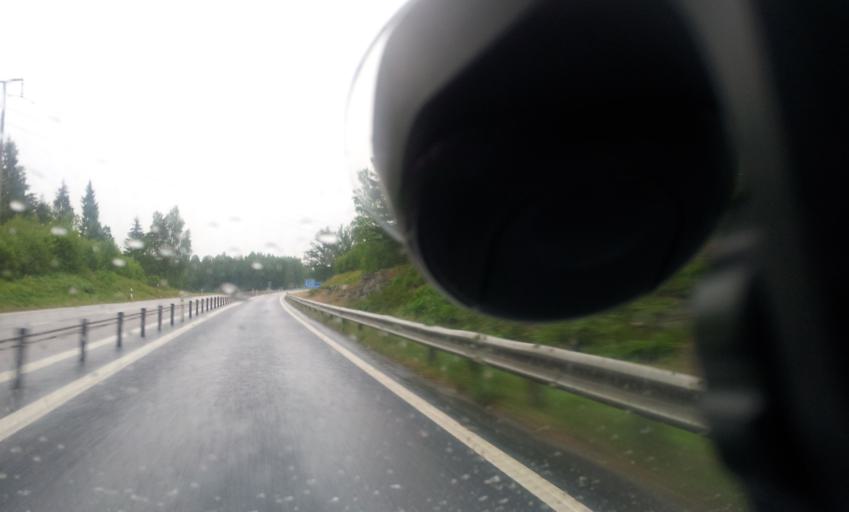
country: SE
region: Kalmar
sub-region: Vasterviks Kommun
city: Forserum
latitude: 58.0703
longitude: 16.5202
